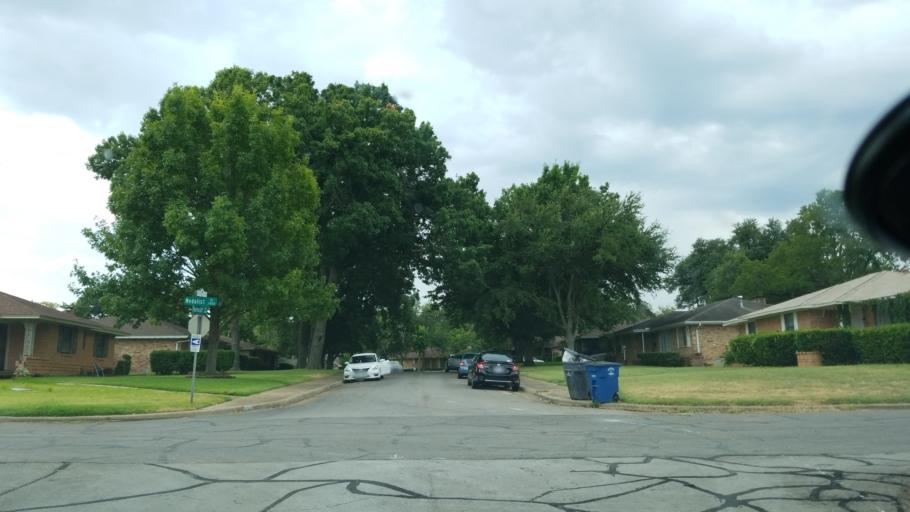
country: US
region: Texas
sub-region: Dallas County
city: Duncanville
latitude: 32.6678
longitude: -96.8394
